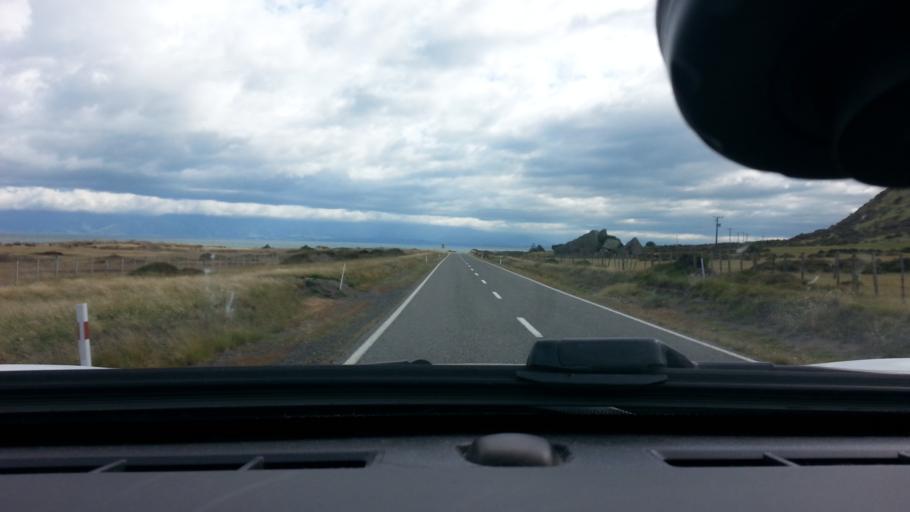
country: NZ
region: Wellington
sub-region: South Wairarapa District
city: Waipawa
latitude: -41.5249
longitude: 175.1996
